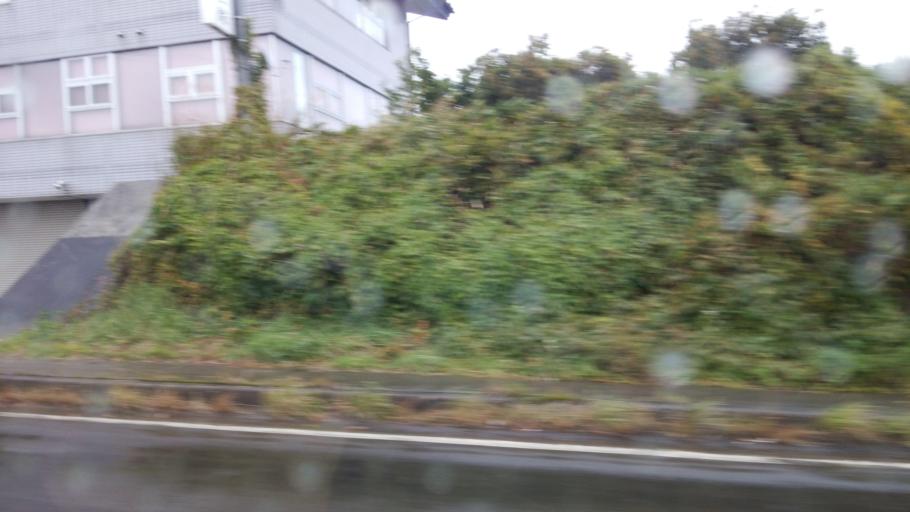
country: JP
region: Fukushima
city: Kitakata
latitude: 37.5318
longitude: 139.9444
